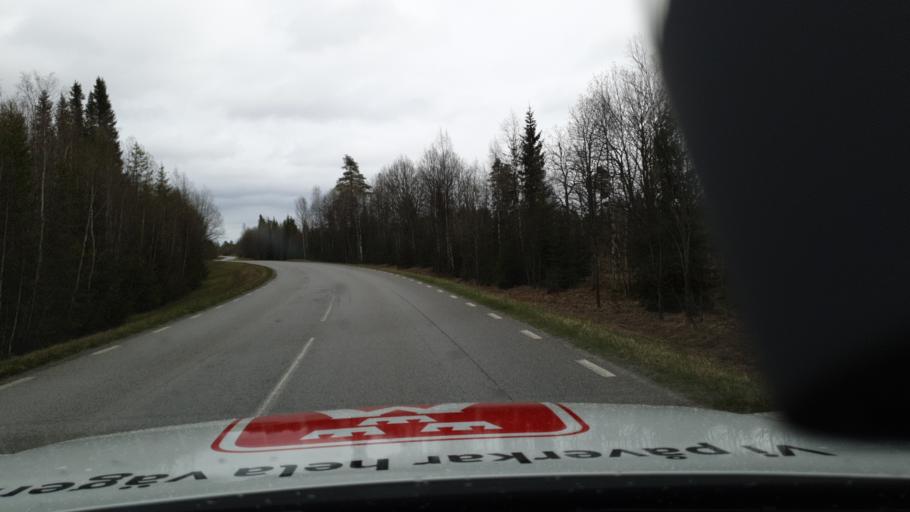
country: SE
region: Jaemtland
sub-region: Stroemsunds Kommun
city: Stroemsund
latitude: 63.5976
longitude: 15.3135
